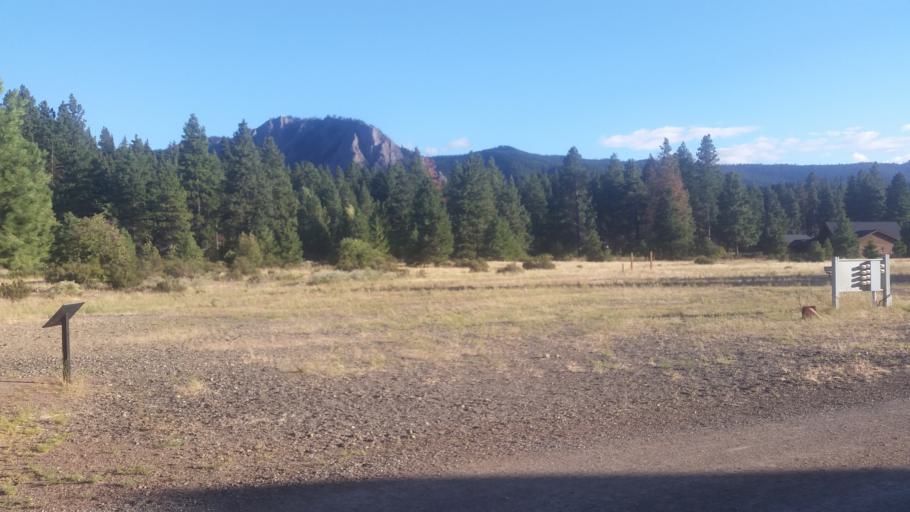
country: US
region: Washington
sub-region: Kittitas County
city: Cle Elum
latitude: 47.1831
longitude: -120.9557
